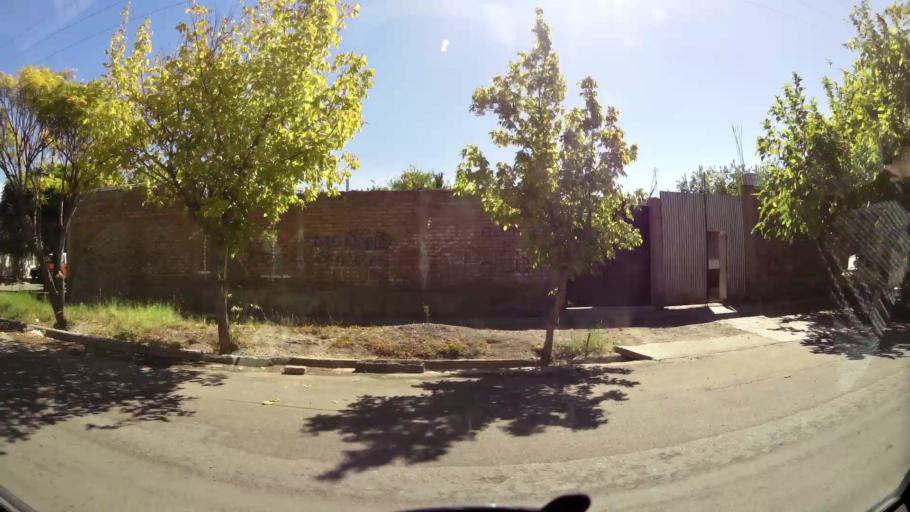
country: AR
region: Mendoza
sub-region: Departamento de Godoy Cruz
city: Godoy Cruz
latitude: -32.9659
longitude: -68.8351
